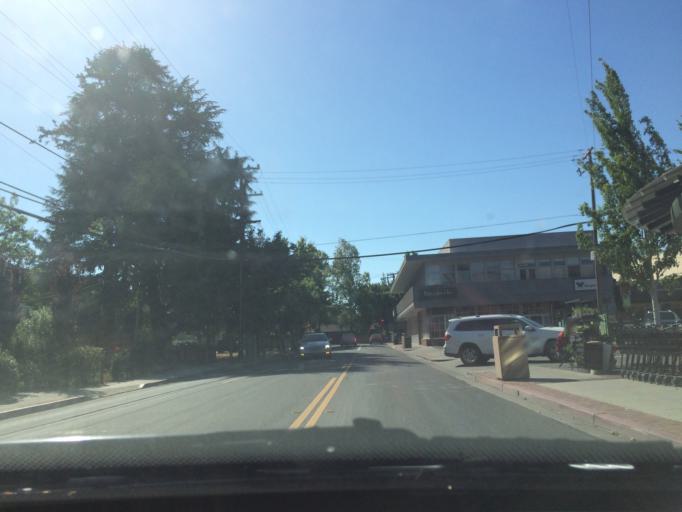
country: US
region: California
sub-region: San Mateo County
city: Menlo Park
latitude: 37.4490
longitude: -122.1855
